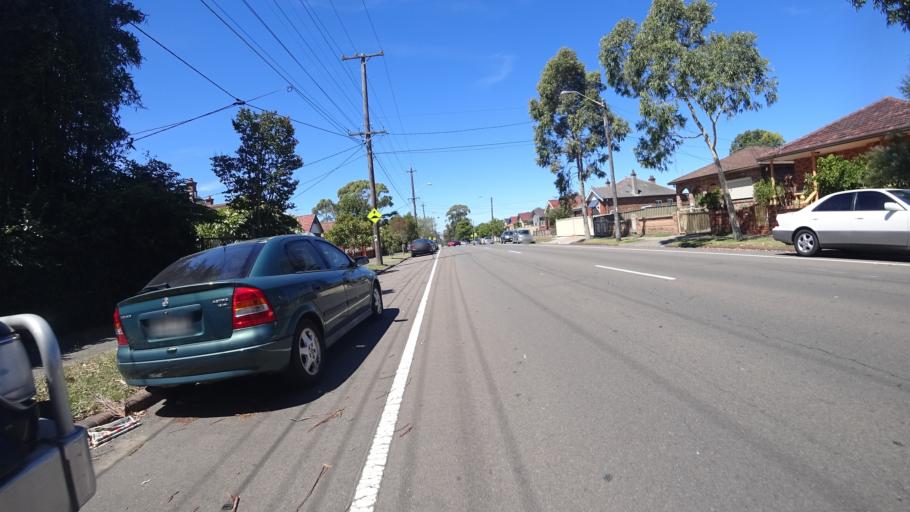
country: AU
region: New South Wales
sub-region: Rockdale
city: Bardwell Valley
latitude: -33.9408
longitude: 151.1338
